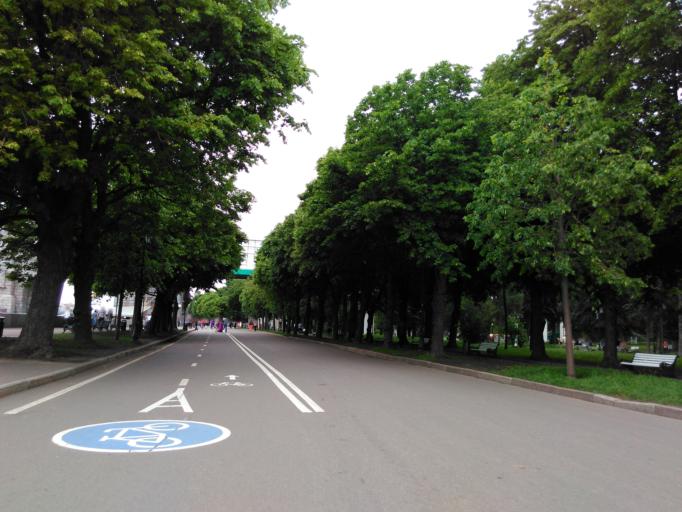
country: RU
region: Moscow
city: Novyye Cheremushki
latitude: 55.7231
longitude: 37.5924
